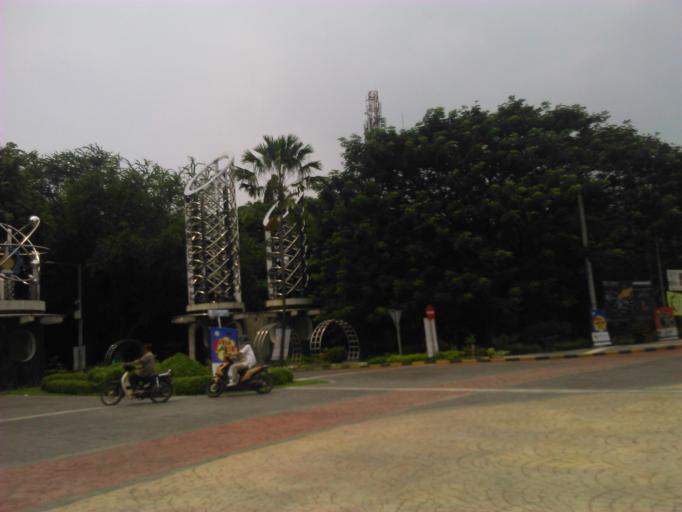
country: ID
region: East Java
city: Mulyorejo
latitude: -7.2794
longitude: 112.7908
